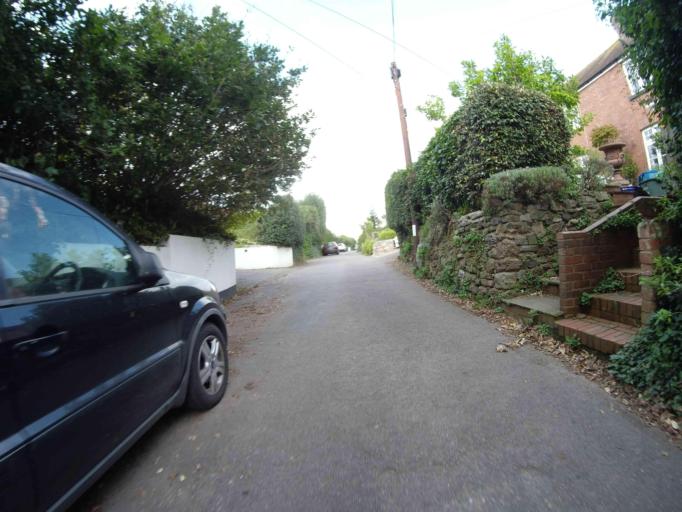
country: GB
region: England
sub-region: Devon
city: Budleigh Salterton
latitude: 50.6332
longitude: -3.3150
